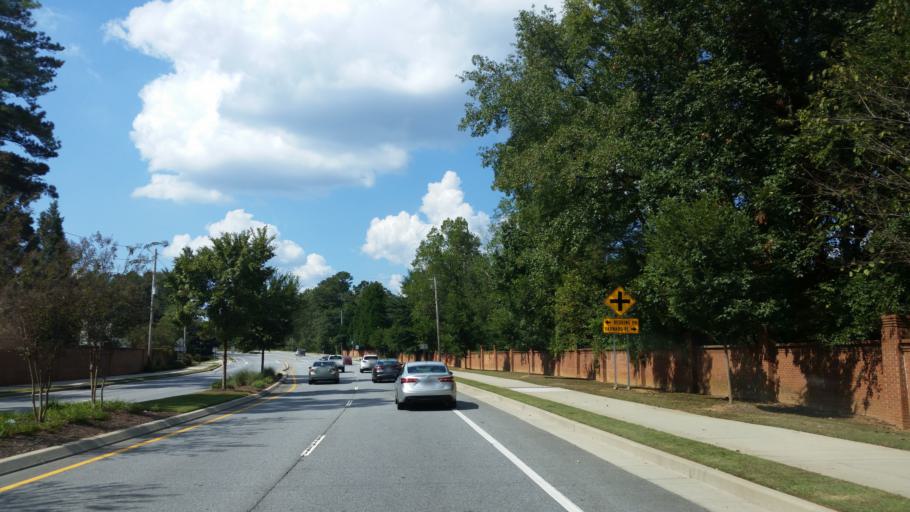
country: US
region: Georgia
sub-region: Fulton County
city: Sandy Springs
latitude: 33.9371
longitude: -84.3933
